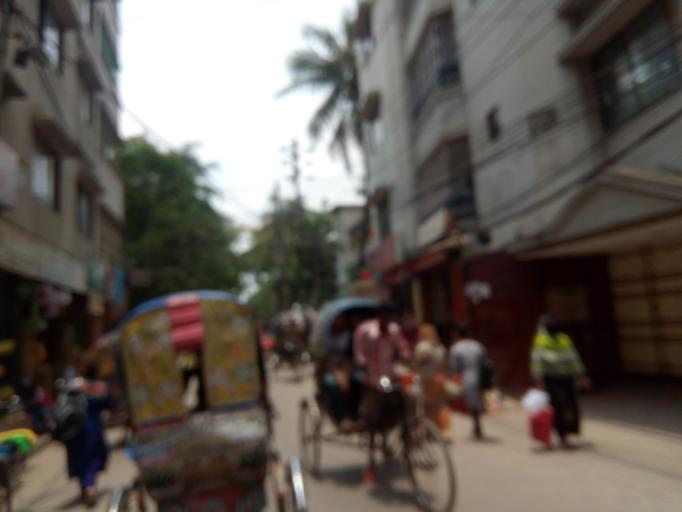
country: BD
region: Dhaka
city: Paltan
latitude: 23.7514
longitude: 90.4095
